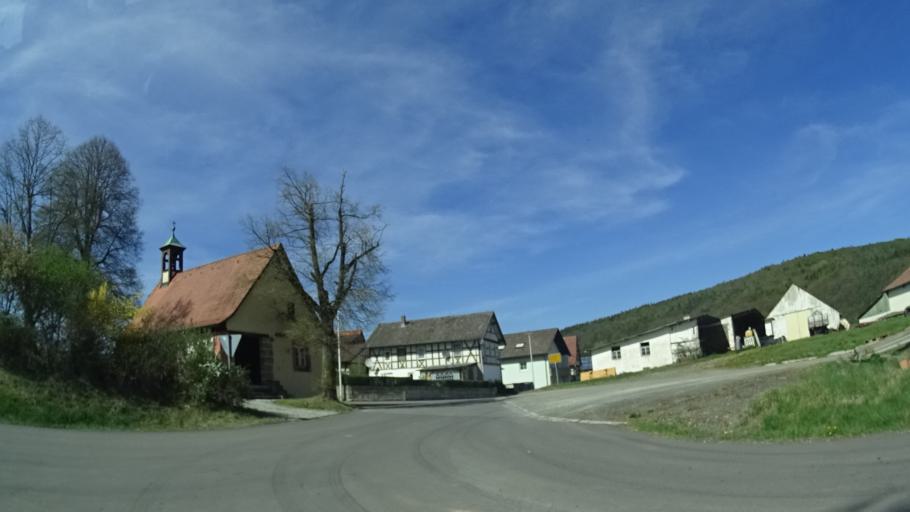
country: DE
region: Bavaria
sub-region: Regierungsbezirk Unterfranken
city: Burgpreppach
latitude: 50.1585
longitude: 10.5942
